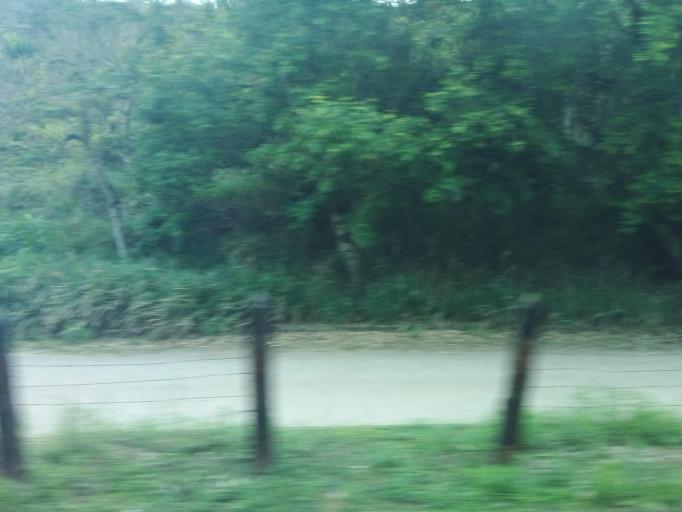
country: BR
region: Minas Gerais
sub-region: Nova Era
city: Nova Era
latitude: -19.7283
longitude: -42.9963
